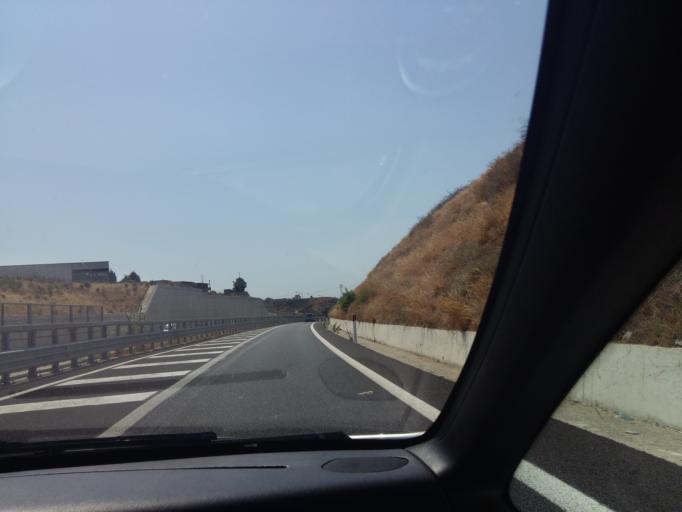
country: IT
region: Calabria
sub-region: Provincia di Reggio Calabria
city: Campo Calabro
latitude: 38.2167
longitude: 15.6477
